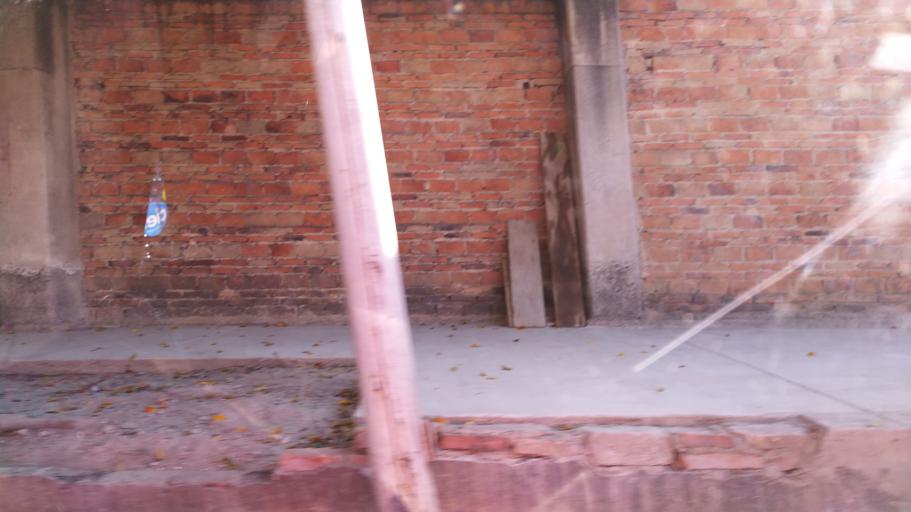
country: MX
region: Jalisco
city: Zapopan2
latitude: 20.7011
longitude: -103.4004
